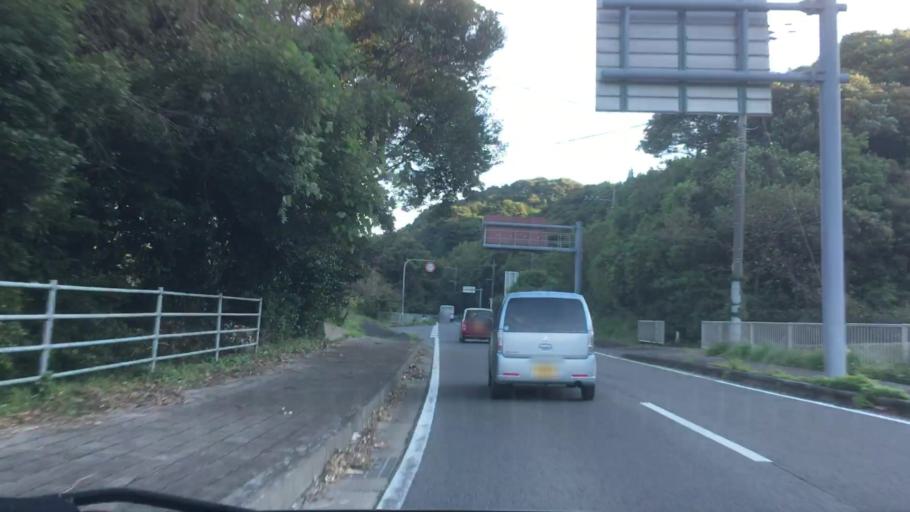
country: JP
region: Nagasaki
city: Sasebo
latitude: 33.0384
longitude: 129.6594
